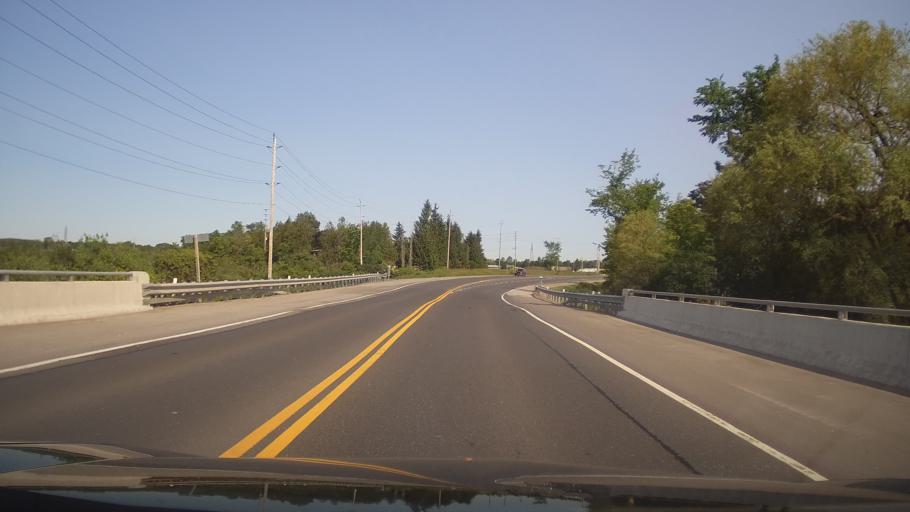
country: CA
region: Ontario
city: Peterborough
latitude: 44.2769
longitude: -78.4168
